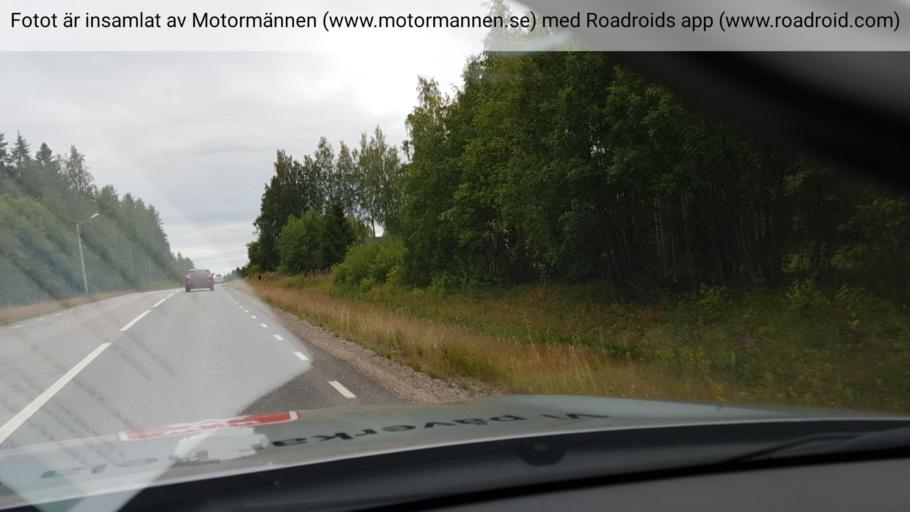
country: SE
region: Norrbotten
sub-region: Overkalix Kommun
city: OEverkalix
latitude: 66.5332
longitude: 22.7569
